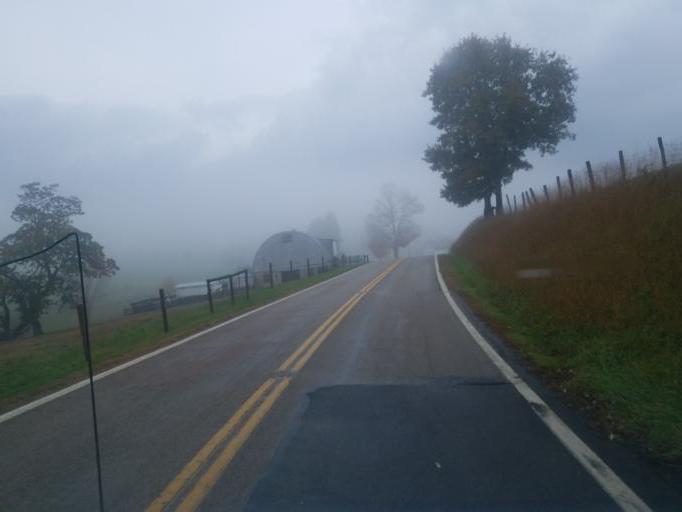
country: US
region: Ohio
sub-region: Morgan County
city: McConnelsville
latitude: 39.5147
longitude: -81.9178
